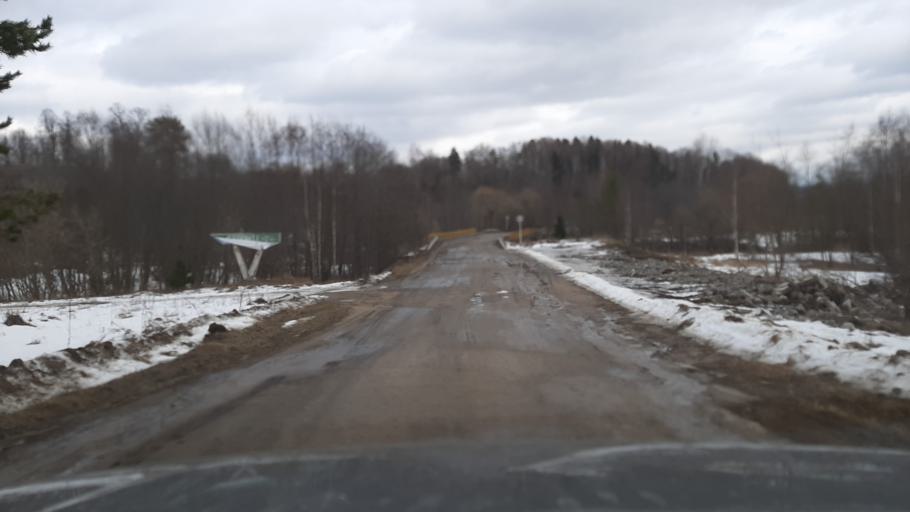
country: RU
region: Ivanovo
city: Teykovo
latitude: 56.8945
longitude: 40.6624
